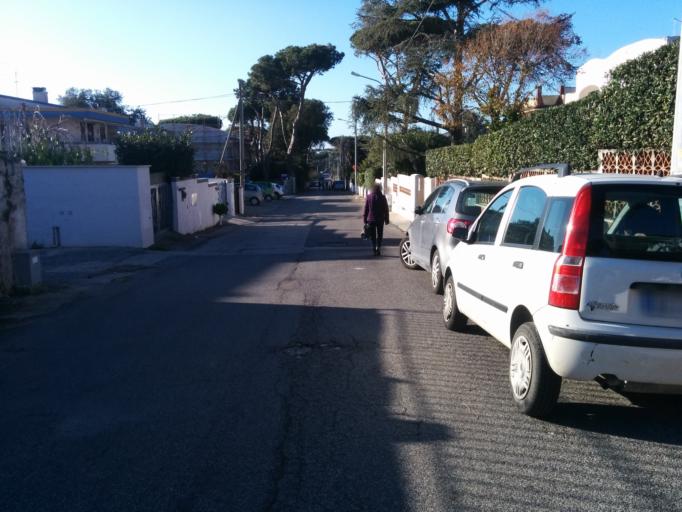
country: IT
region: Latium
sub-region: Citta metropolitana di Roma Capitale
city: Lavinio
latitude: 41.4992
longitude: 12.5970
